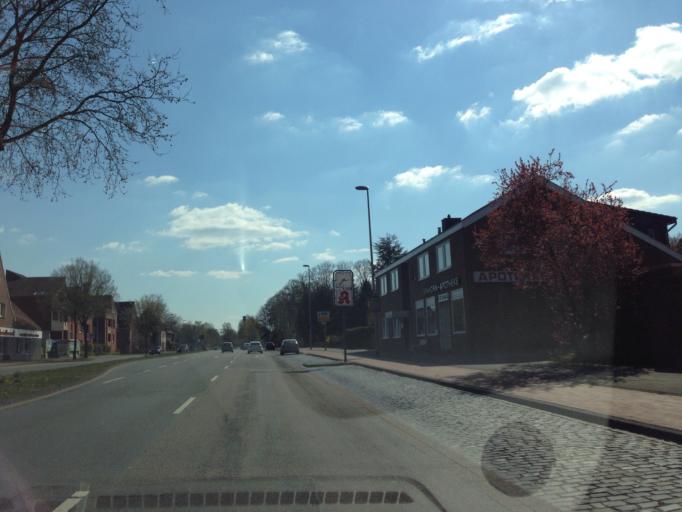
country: DE
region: North Rhine-Westphalia
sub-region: Regierungsbezirk Munster
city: Muenster
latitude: 51.9948
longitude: 7.6126
